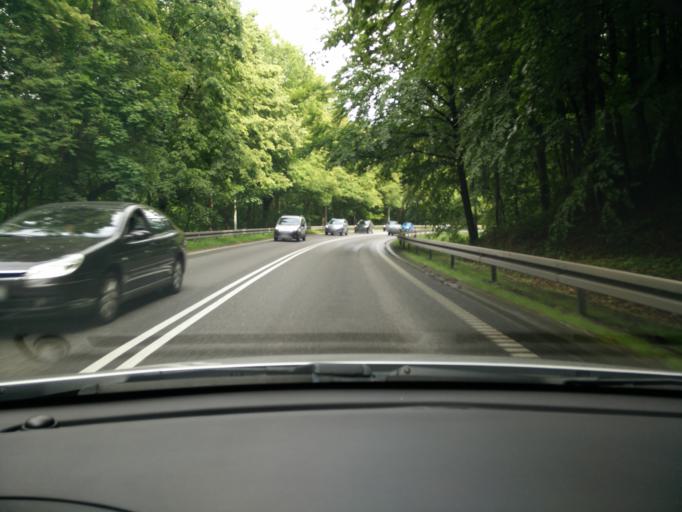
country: PL
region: Pomeranian Voivodeship
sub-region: Gdynia
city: Wielki Kack
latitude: 54.4288
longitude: 18.4993
